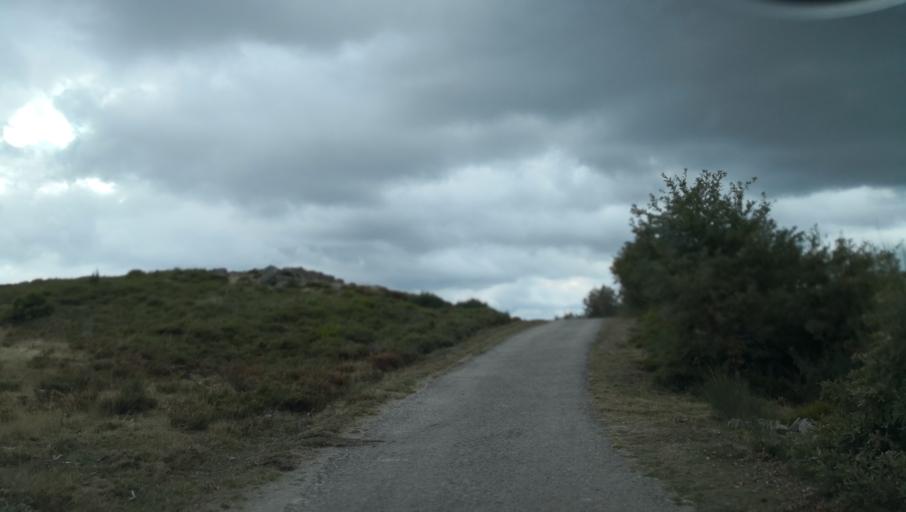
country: PT
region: Vila Real
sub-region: Vila Real
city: Vila Real
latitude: 41.3830
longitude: -7.8069
